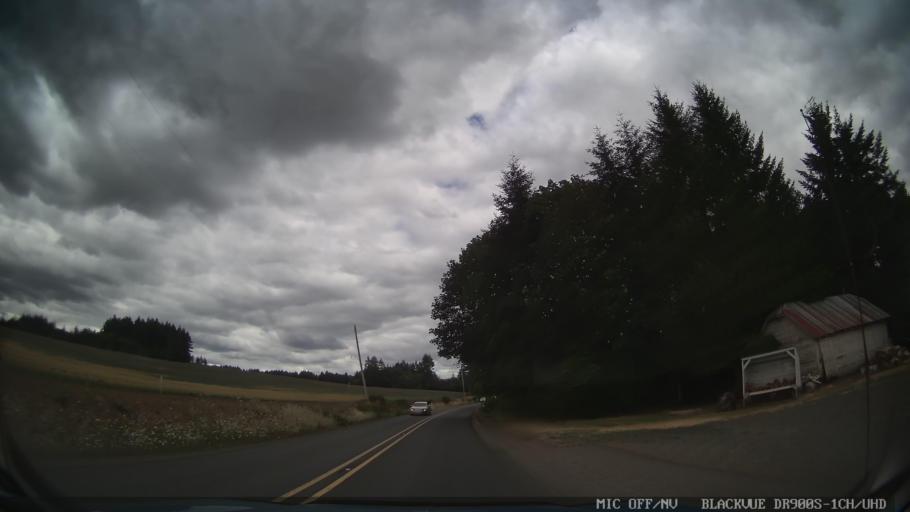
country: US
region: Oregon
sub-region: Linn County
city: Lyons
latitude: 44.8508
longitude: -122.6764
